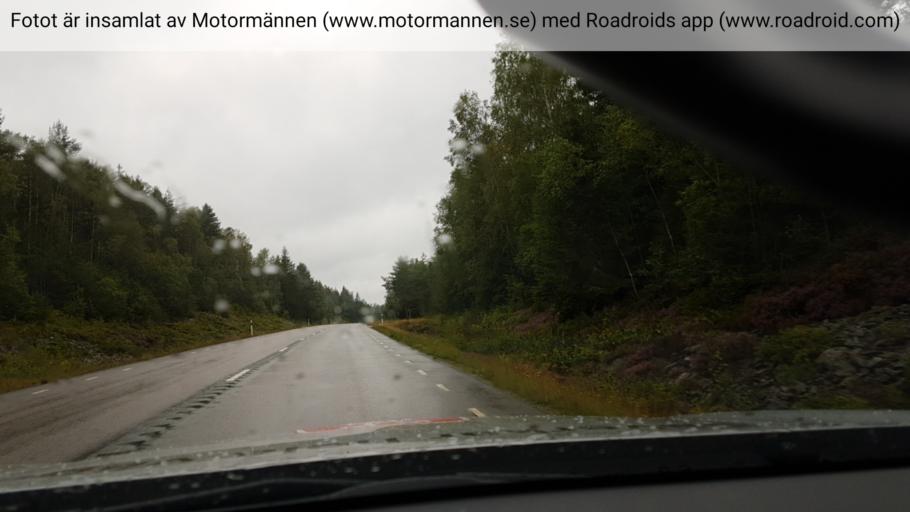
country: SE
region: Vaestra Goetaland
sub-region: Bengtsfors Kommun
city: Billingsfors
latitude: 58.9325
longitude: 12.1773
